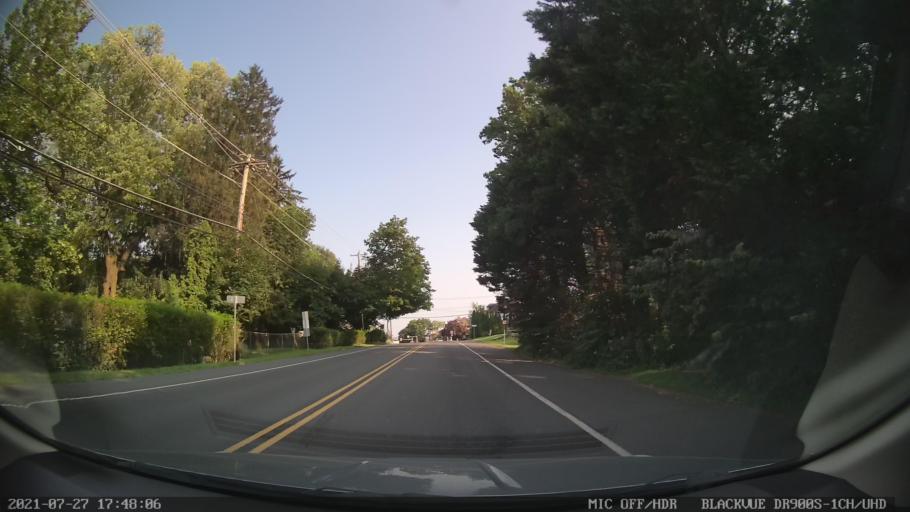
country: US
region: Pennsylvania
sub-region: Berks County
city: West Reading
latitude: 40.3595
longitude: -75.9518
